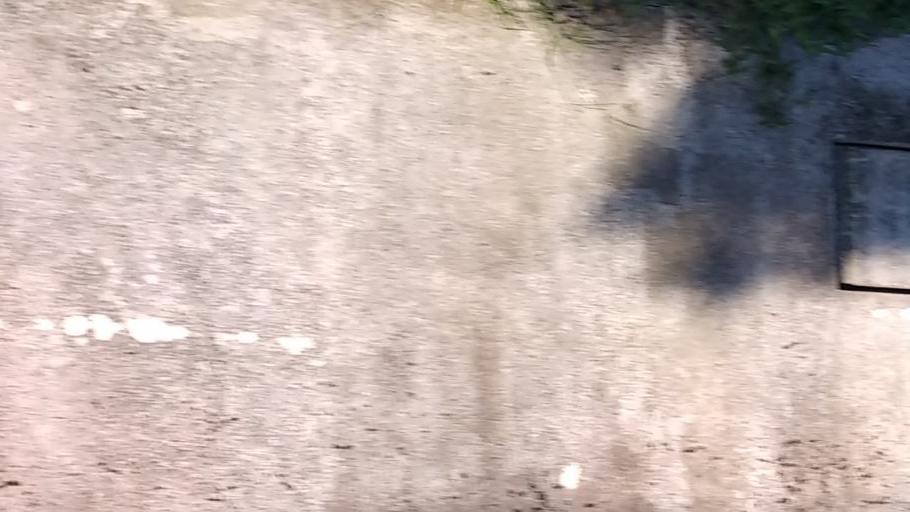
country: FR
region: Midi-Pyrenees
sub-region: Departement de la Haute-Garonne
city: Cugnaux
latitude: 43.5618
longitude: 1.3706
